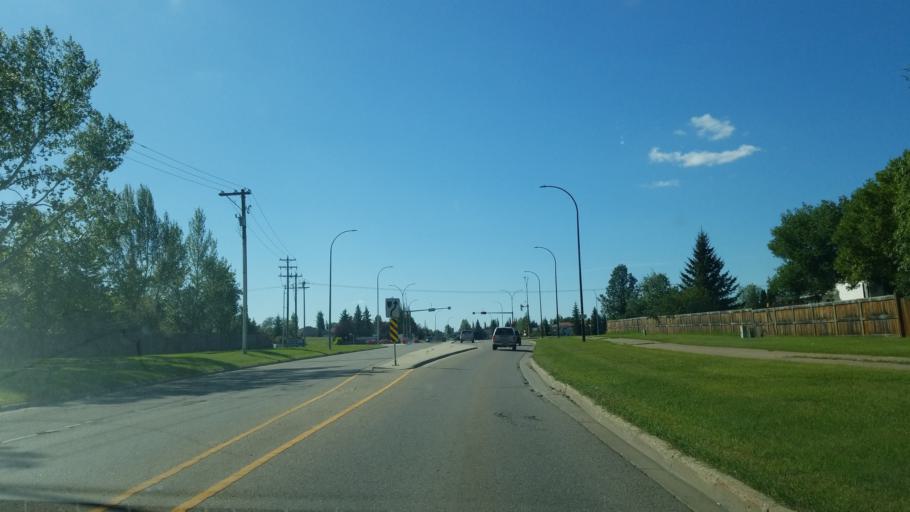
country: CA
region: Saskatchewan
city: Lloydminster
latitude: 53.2707
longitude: -110.0274
